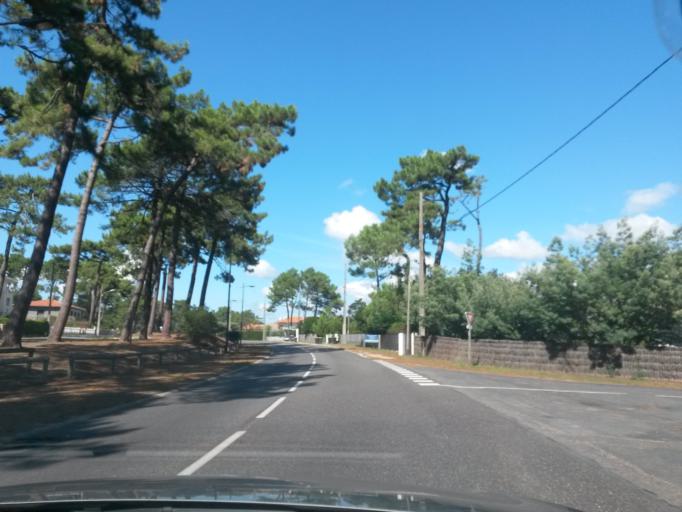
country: FR
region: Aquitaine
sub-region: Departement de la Gironde
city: Arcachon
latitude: 44.7059
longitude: -1.2249
